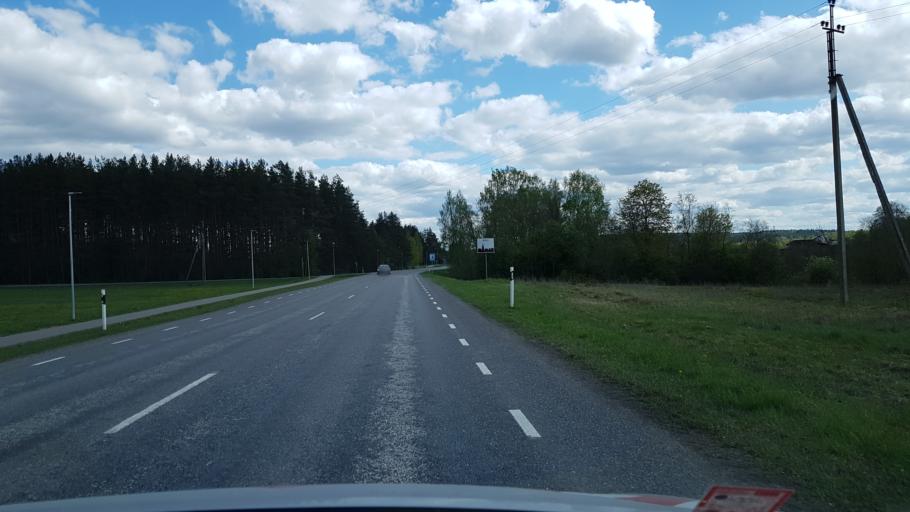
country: EE
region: Tartu
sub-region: UElenurme vald
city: Ulenurme
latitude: 58.3038
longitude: 26.8611
